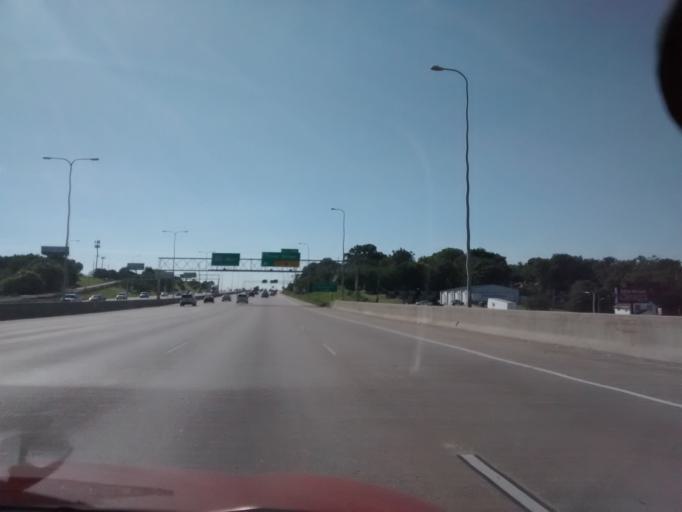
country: US
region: Nebraska
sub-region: Douglas County
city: Ralston
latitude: 41.2239
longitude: -96.0126
